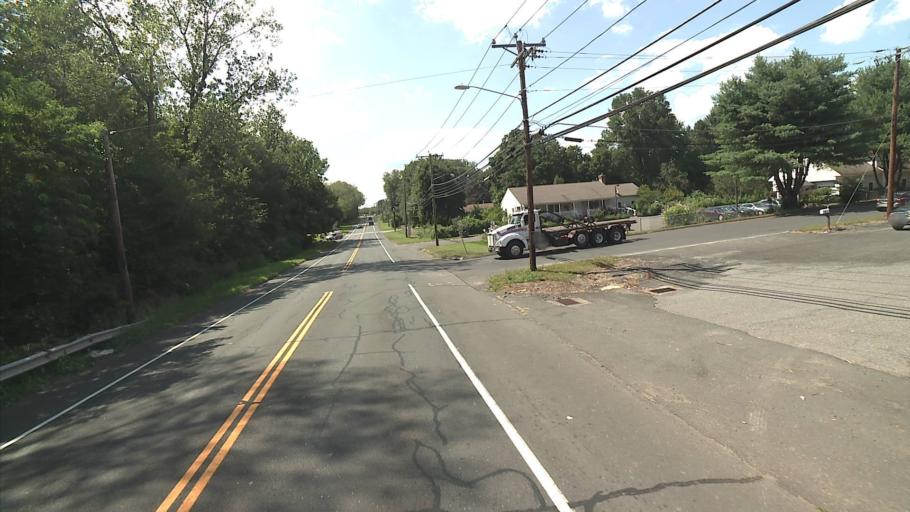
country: US
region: Connecticut
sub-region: Hartford County
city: Hazardville
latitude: 41.9850
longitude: -72.5057
